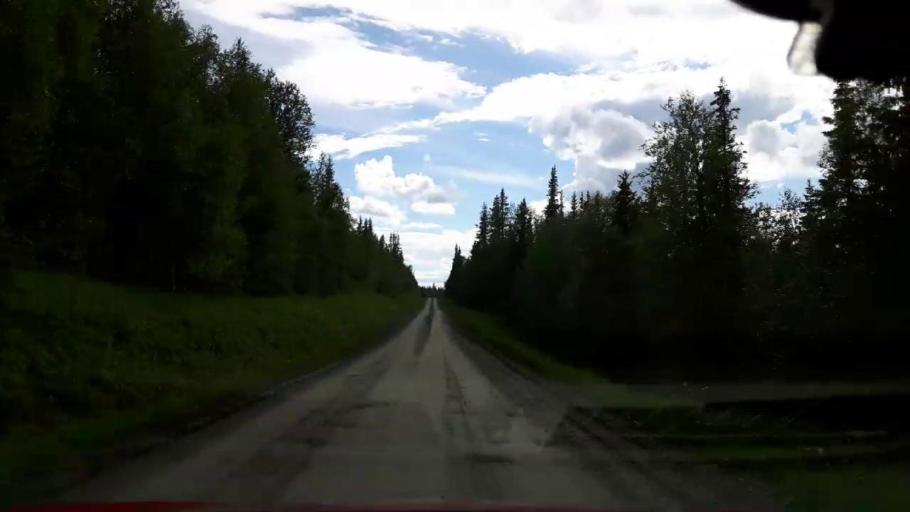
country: SE
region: Jaemtland
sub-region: Krokoms Kommun
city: Valla
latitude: 63.8648
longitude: 14.1137
